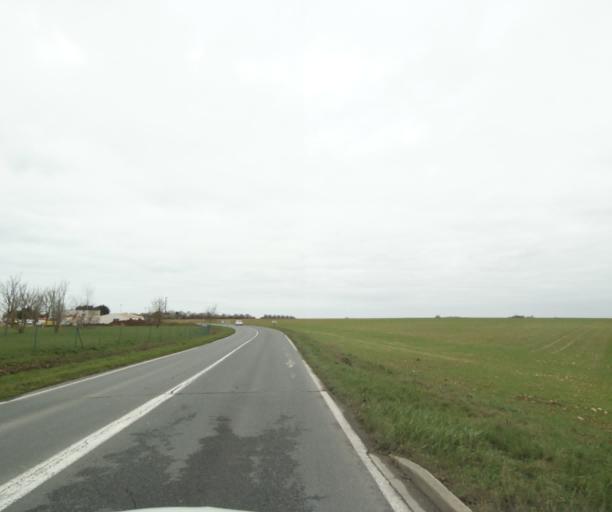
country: FR
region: Poitou-Charentes
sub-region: Departement de la Charente-Maritime
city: Lagord
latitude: 46.1920
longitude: -1.1476
